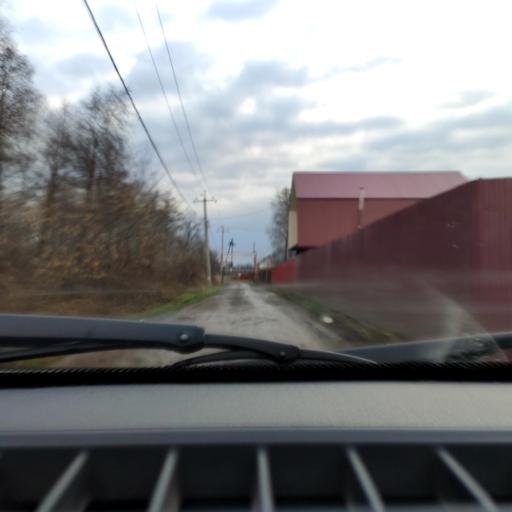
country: RU
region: Bashkortostan
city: Avdon
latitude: 54.6247
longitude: 55.7346
